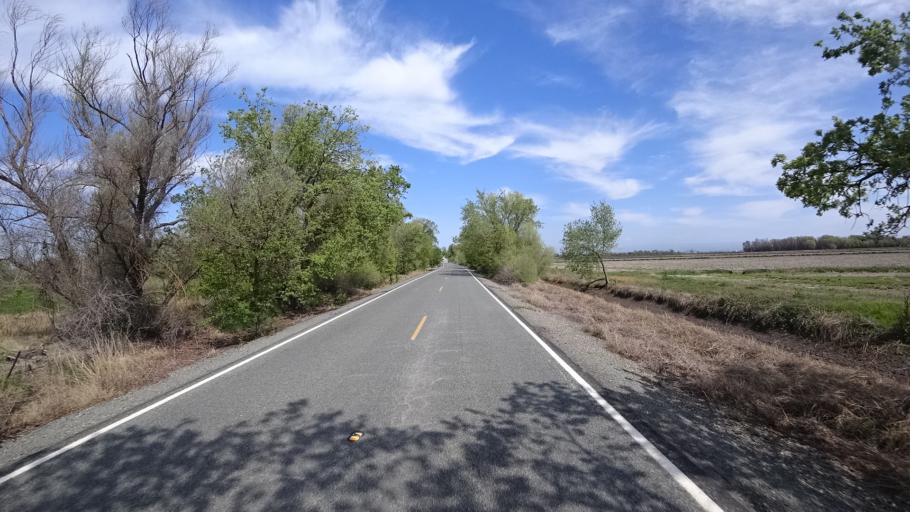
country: US
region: California
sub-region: Butte County
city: Durham
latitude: 39.5239
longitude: -121.8567
